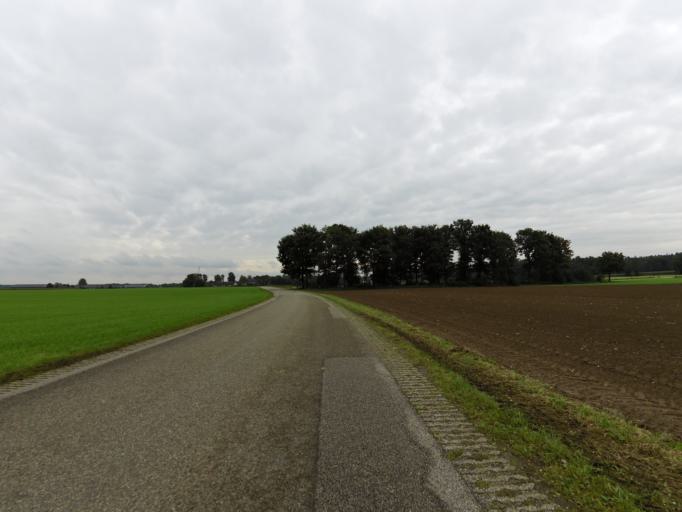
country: NL
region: Gelderland
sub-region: Oude IJsselstreek
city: Gendringen
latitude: 51.8746
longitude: 6.4115
